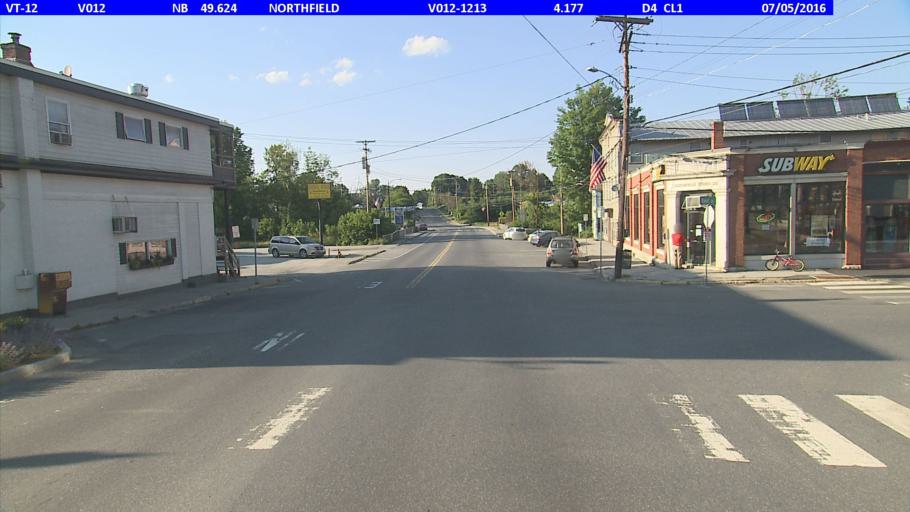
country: US
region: Vermont
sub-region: Washington County
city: Northfield
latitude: 44.1487
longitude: -72.6561
